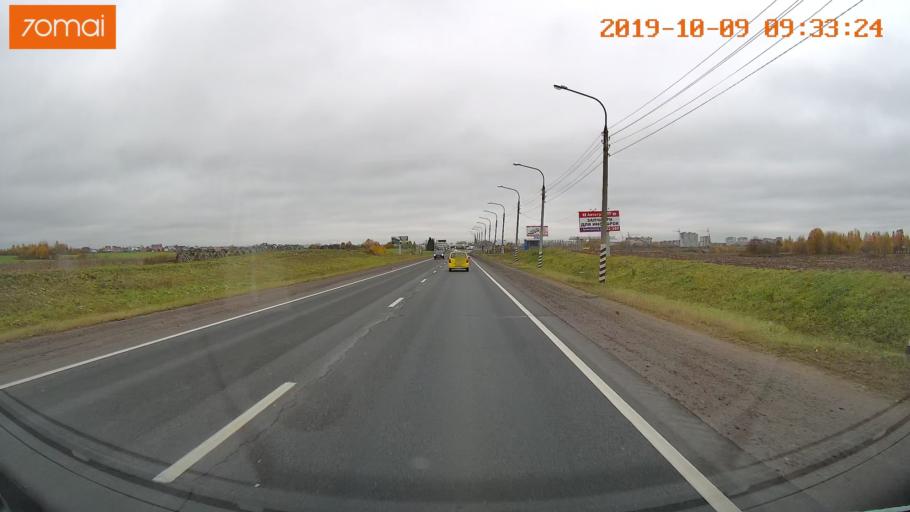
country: RU
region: Vologda
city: Vologda
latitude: 59.1679
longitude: 39.9146
